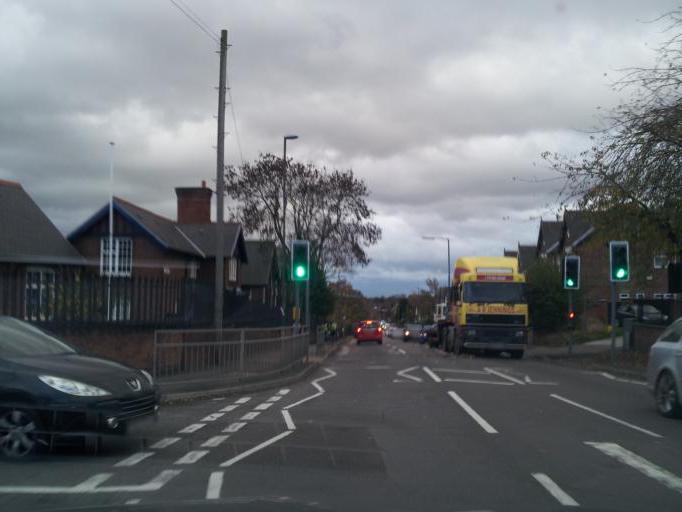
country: GB
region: England
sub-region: Derbyshire
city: Ilkeston
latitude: 52.9830
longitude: -1.3143
